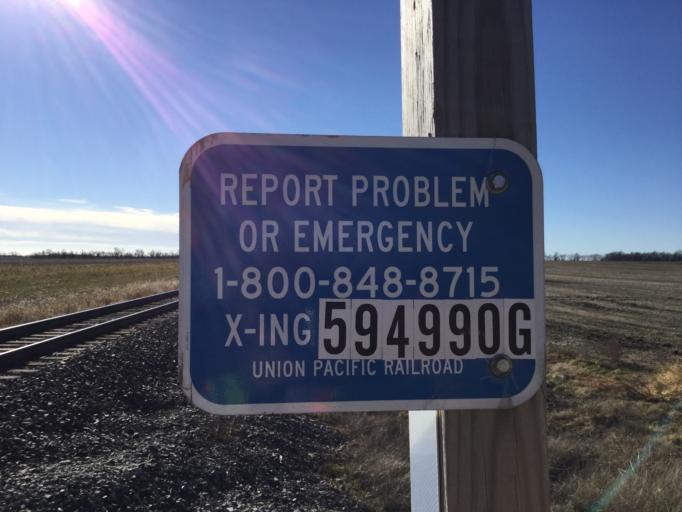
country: US
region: Kansas
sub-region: Marion County
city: Peabody
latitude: 38.0147
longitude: -97.1254
